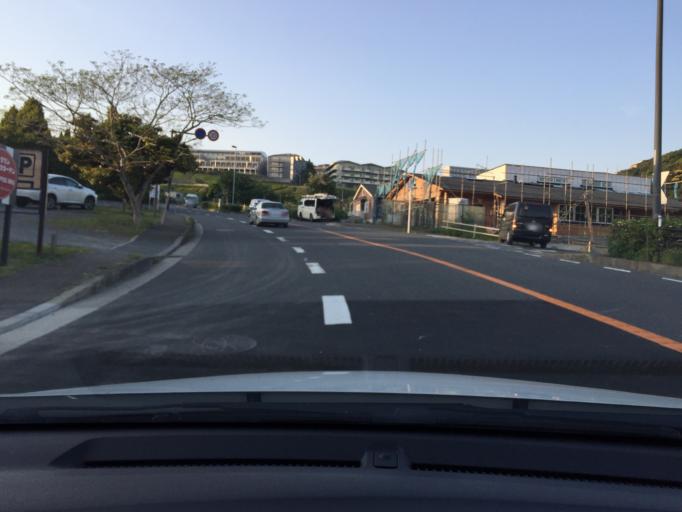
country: JP
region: Kanagawa
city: Hayama
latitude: 35.2514
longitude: 139.6063
